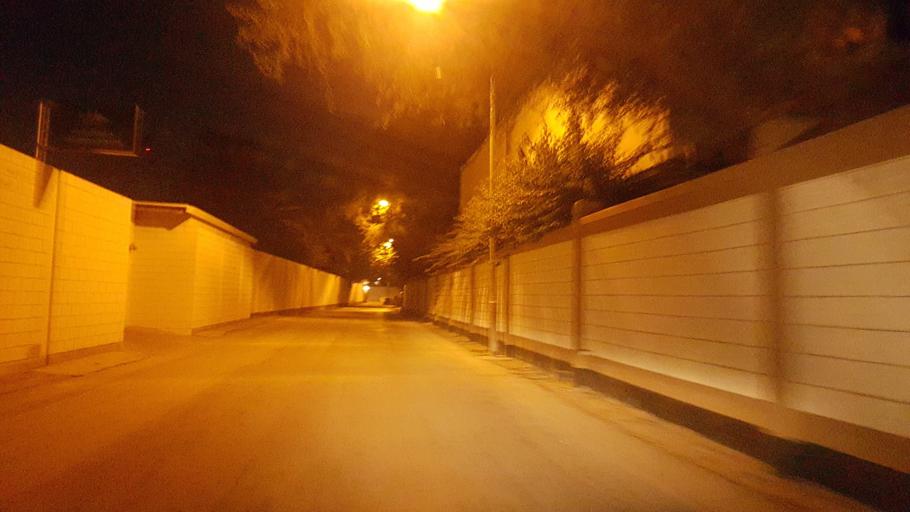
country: BH
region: Manama
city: Jidd Hafs
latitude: 26.2236
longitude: 50.4949
